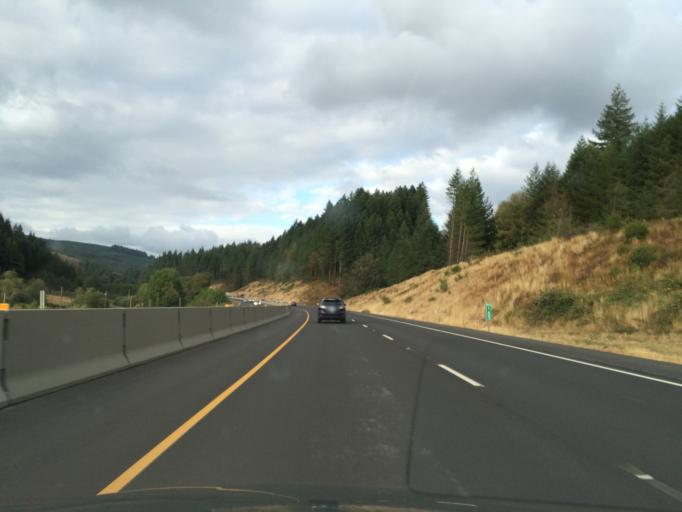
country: US
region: Oregon
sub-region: Lane County
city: Cottage Grove
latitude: 43.7376
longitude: -123.1883
